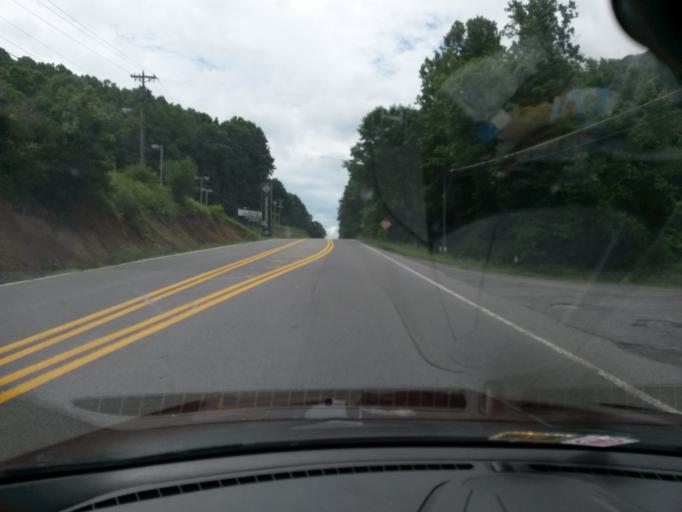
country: US
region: West Virginia
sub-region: Mercer County
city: Brush Fork
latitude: 37.2715
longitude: -81.2447
